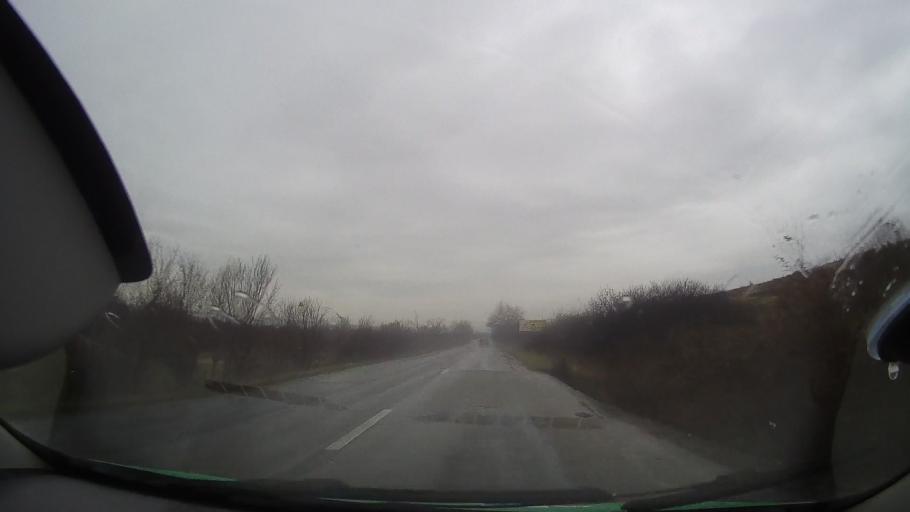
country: RO
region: Bihor
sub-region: Comuna Sambata
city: Sambata
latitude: 46.7770
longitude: 22.1874
